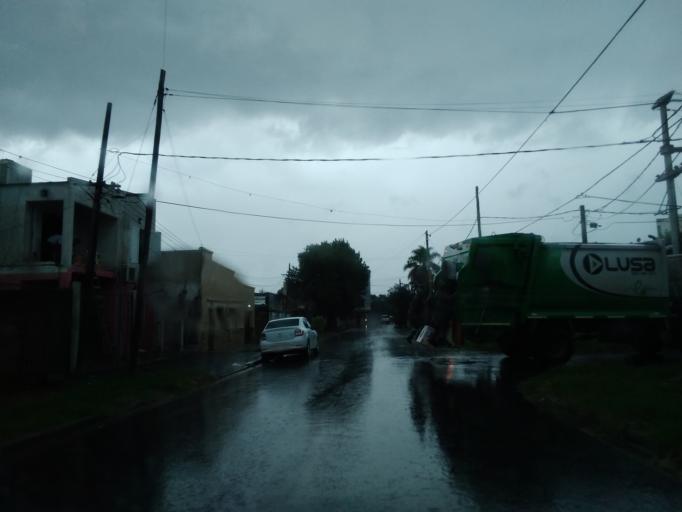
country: AR
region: Corrientes
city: Corrientes
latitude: -27.4904
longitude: -58.8215
